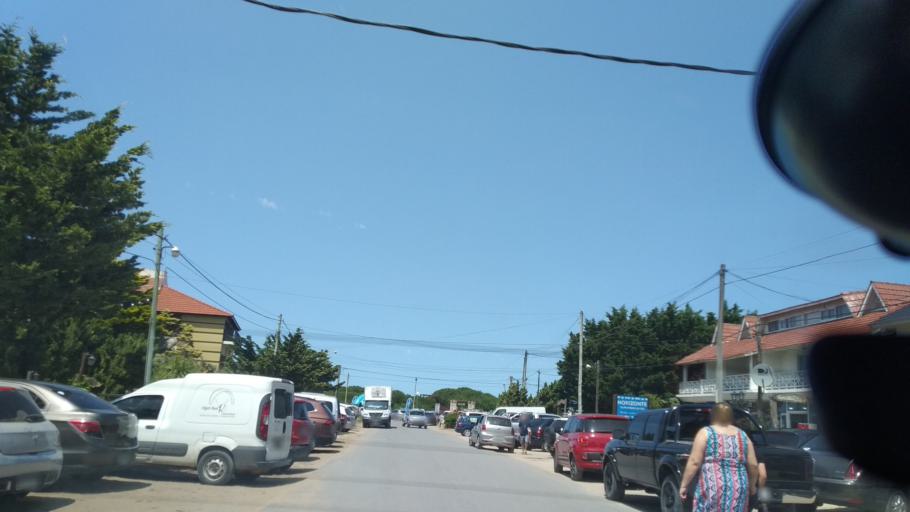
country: AR
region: Buenos Aires
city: Mar del Tuyu
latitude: -36.6065
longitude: -56.6871
